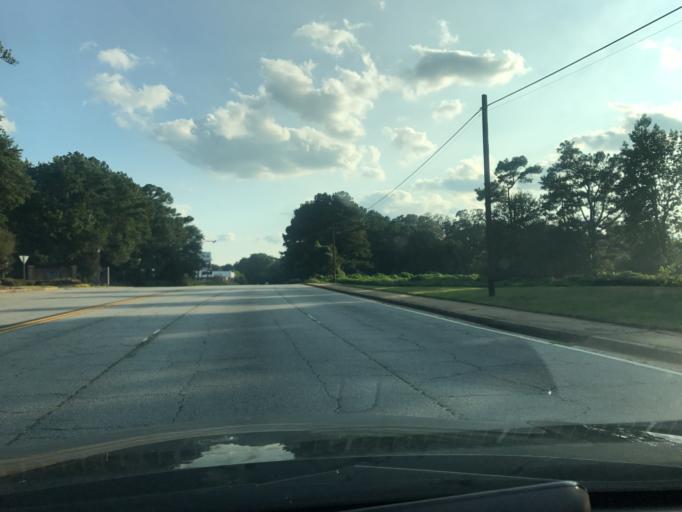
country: US
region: Georgia
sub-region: DeKalb County
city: Avondale Estates
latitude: 33.7811
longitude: -84.2779
